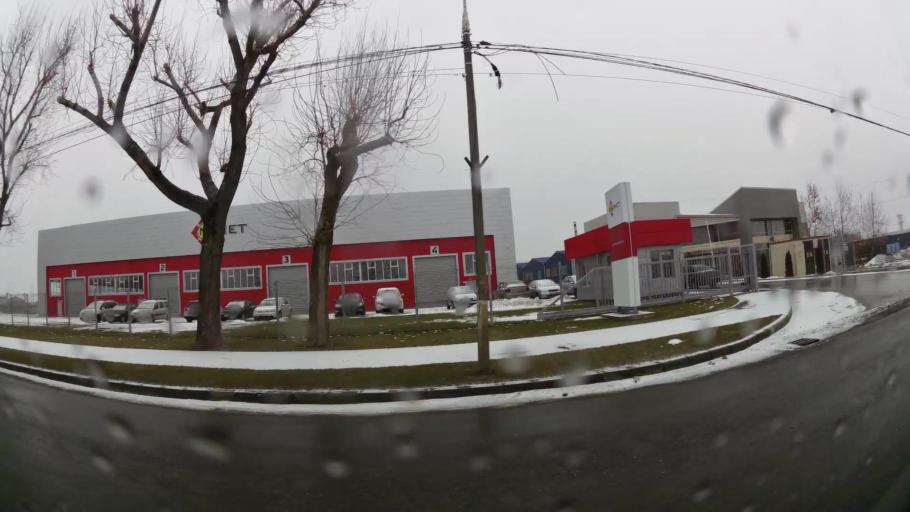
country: RO
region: Dambovita
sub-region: Municipiul Targoviste
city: Targoviste
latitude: 44.9212
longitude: 25.4341
